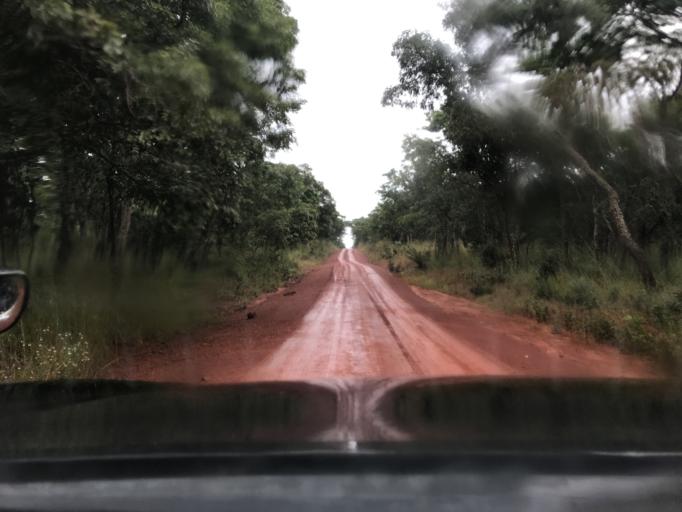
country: TZ
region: Kigoma
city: Uvinza
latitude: -5.2964
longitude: 30.3753
